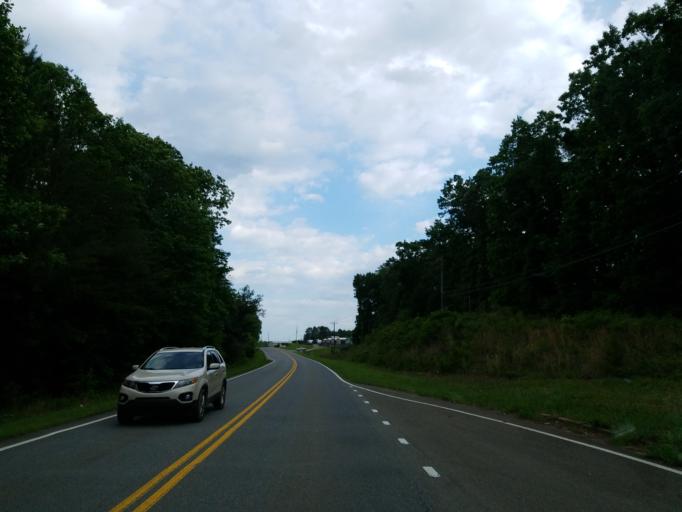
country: US
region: Georgia
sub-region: Pickens County
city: Nelson
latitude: 34.3953
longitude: -84.3816
